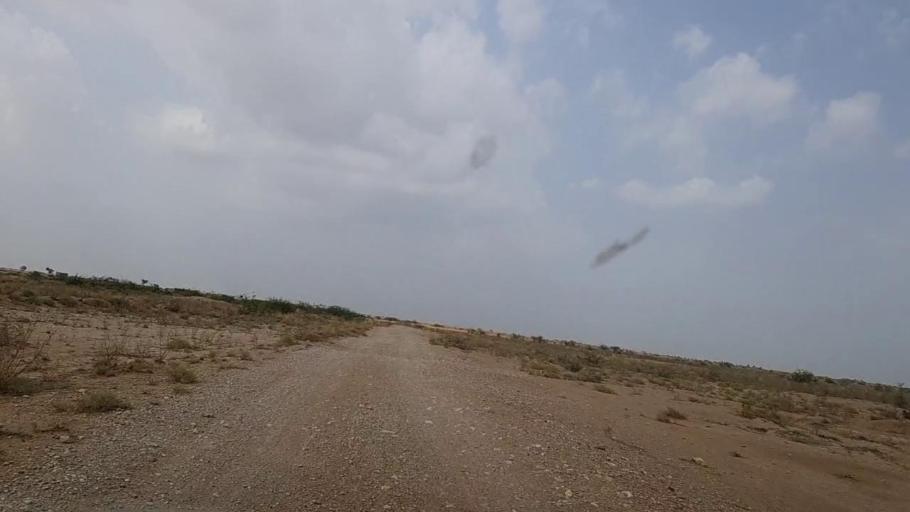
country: PK
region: Sindh
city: Kotri
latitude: 25.2801
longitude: 68.2259
